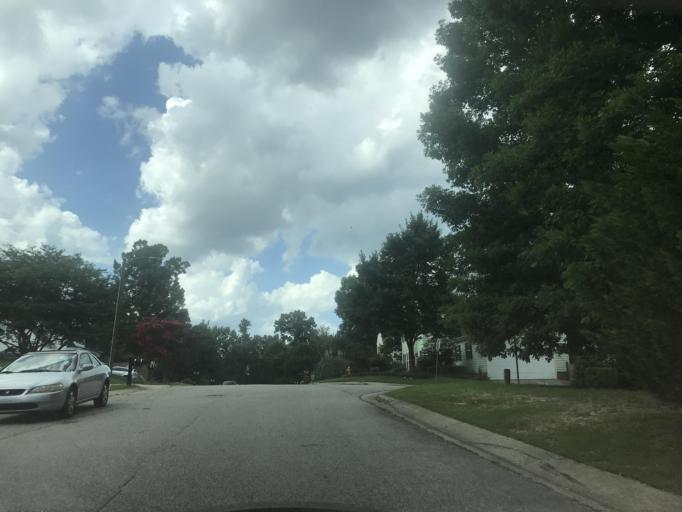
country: US
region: North Carolina
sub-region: Wake County
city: Knightdale
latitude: 35.8367
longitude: -78.5643
